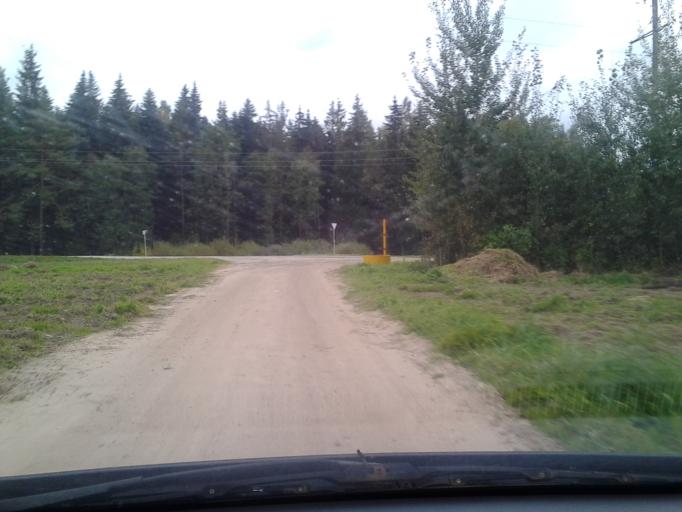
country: BY
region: Vitebsk
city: Pastavy
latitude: 55.1033
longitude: 26.8656
